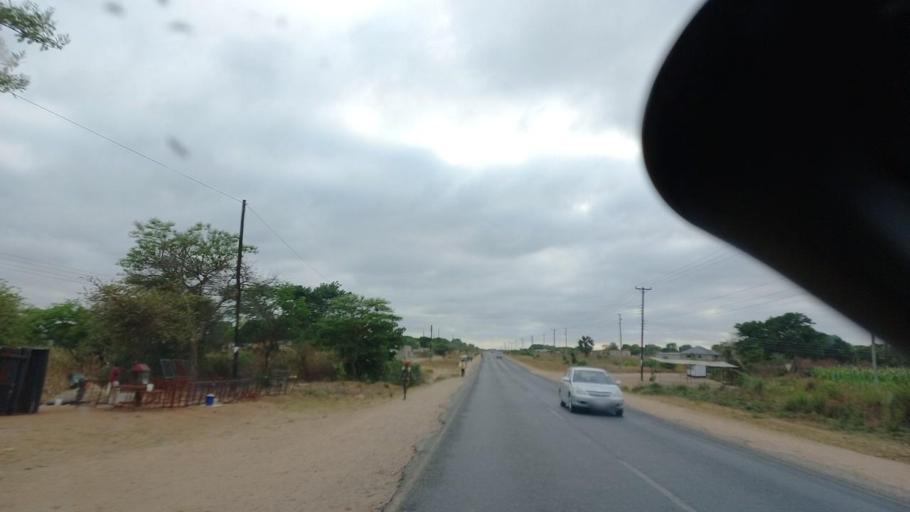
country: ZM
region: Lusaka
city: Chongwe
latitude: -15.3408
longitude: 28.6176
